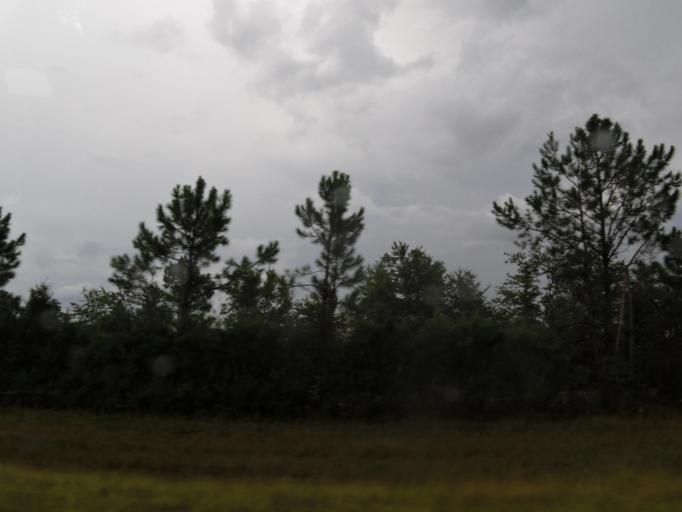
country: US
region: Georgia
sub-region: Wayne County
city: Jesup
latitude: 31.4703
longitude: -81.7204
